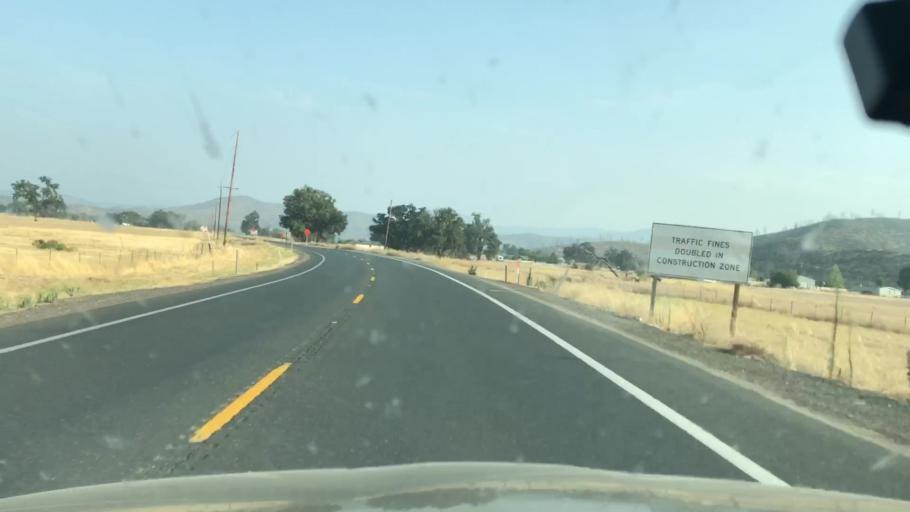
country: US
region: California
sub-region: Lake County
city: Hidden Valley Lake
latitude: 38.8030
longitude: -122.5727
